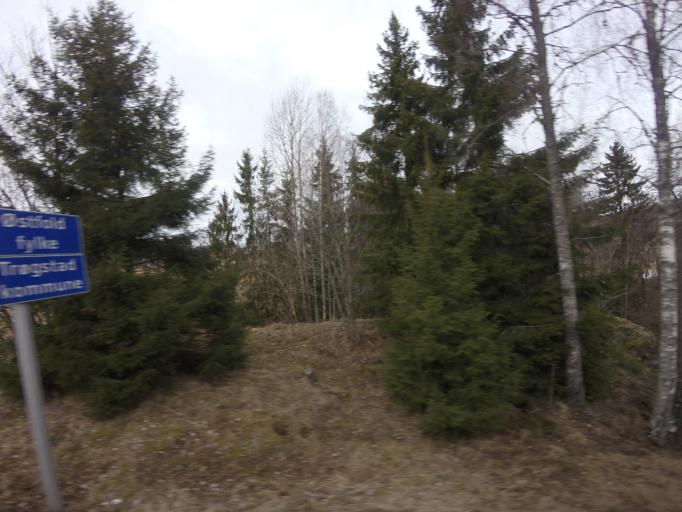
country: NO
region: Ostfold
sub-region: Trogstad
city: Skjonhaug
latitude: 59.7594
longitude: 11.2948
